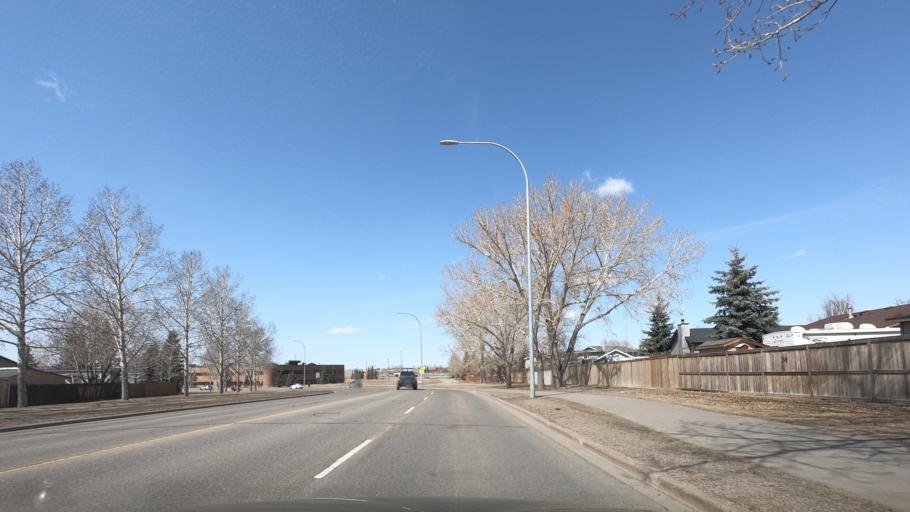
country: CA
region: Alberta
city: Airdrie
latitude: 51.2813
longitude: -113.9898
